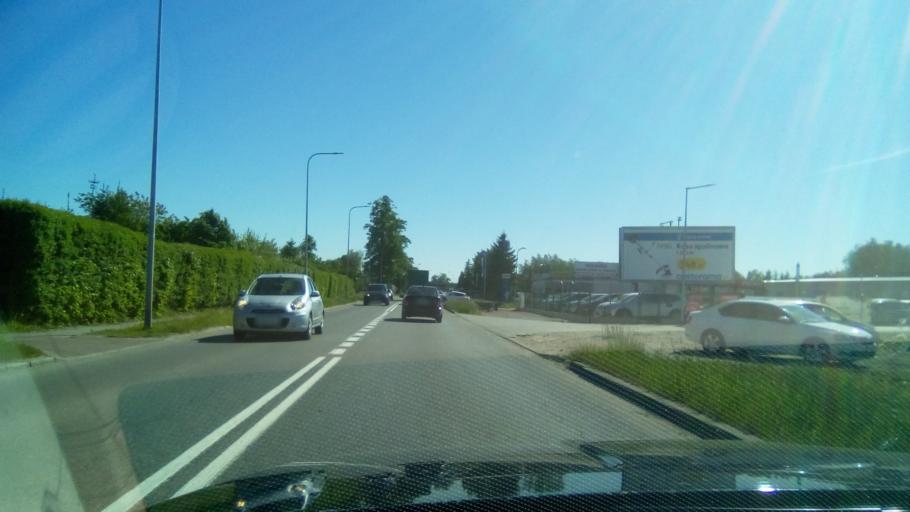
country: PL
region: Warmian-Masurian Voivodeship
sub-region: Powiat elblaski
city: Elblag
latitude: 54.1496
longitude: 19.3901
